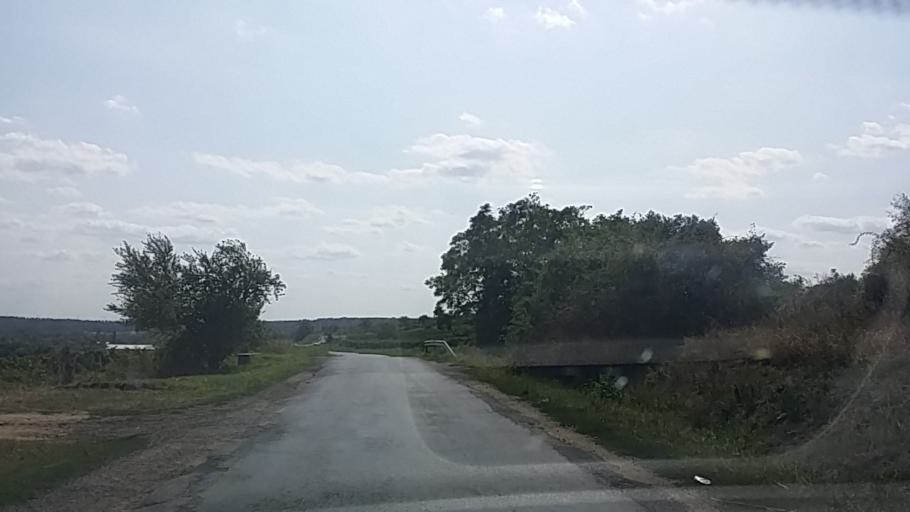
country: HU
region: Gyor-Moson-Sopron
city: Fertorakos
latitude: 47.6656
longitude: 16.6693
